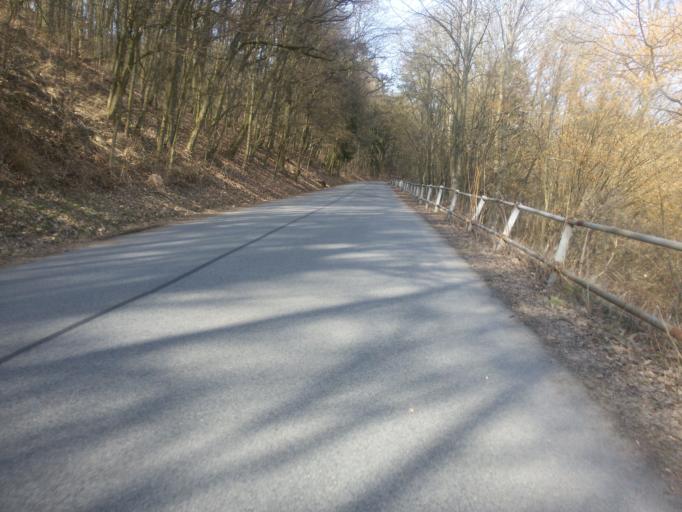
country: CZ
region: South Moravian
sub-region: Okres Brno-Venkov
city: Lomnice
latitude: 49.4190
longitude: 16.4085
